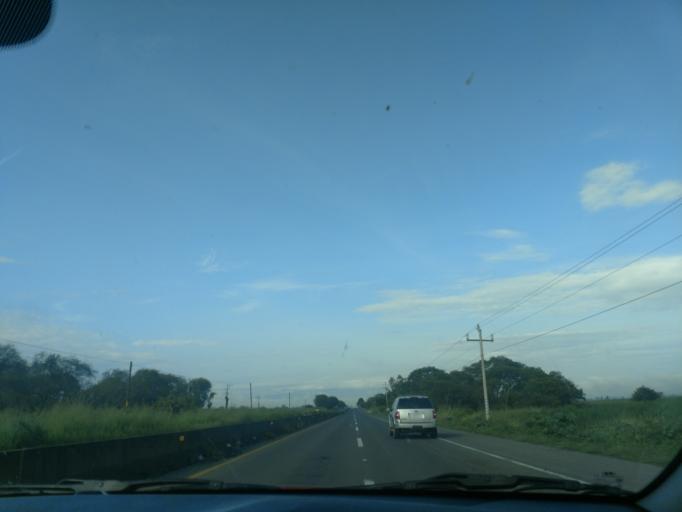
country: MX
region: Jalisco
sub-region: Ameca
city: Los Pocitos
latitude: 20.5500
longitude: -103.9001
